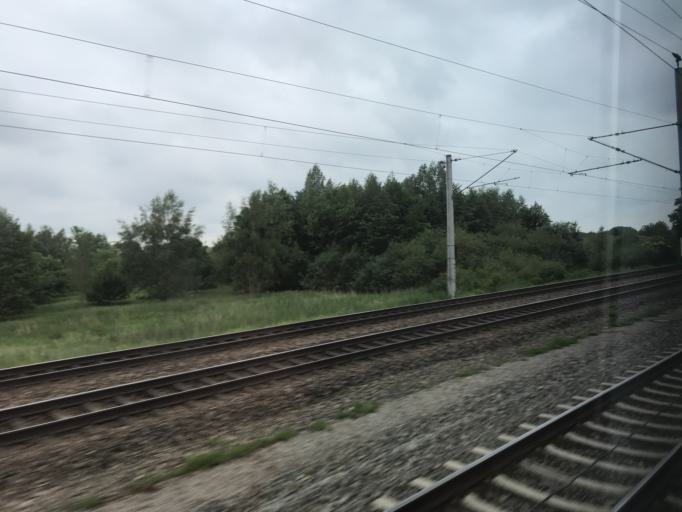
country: DE
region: Bavaria
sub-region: Upper Bavaria
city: Mammendorf
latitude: 48.2176
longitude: 11.1566
